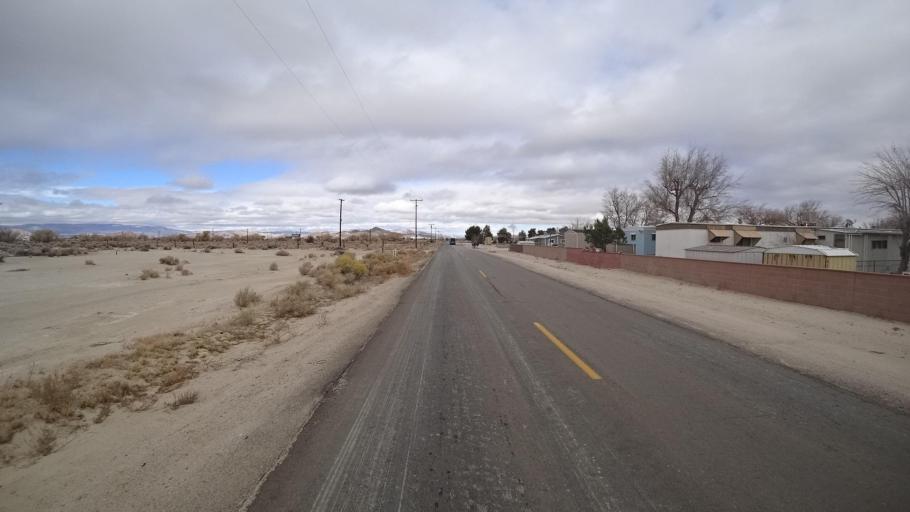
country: US
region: California
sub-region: Kern County
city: Rosamond
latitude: 34.8273
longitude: -118.1670
